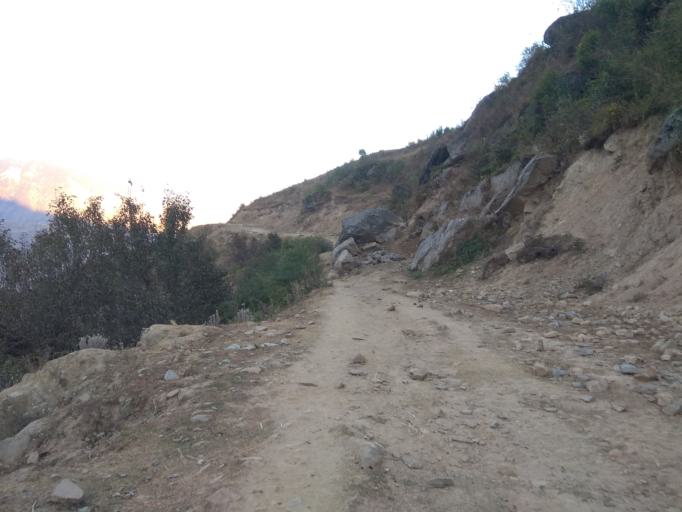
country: NP
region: Mid Western
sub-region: Karnali Zone
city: Jumla
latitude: 29.3140
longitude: 81.7280
